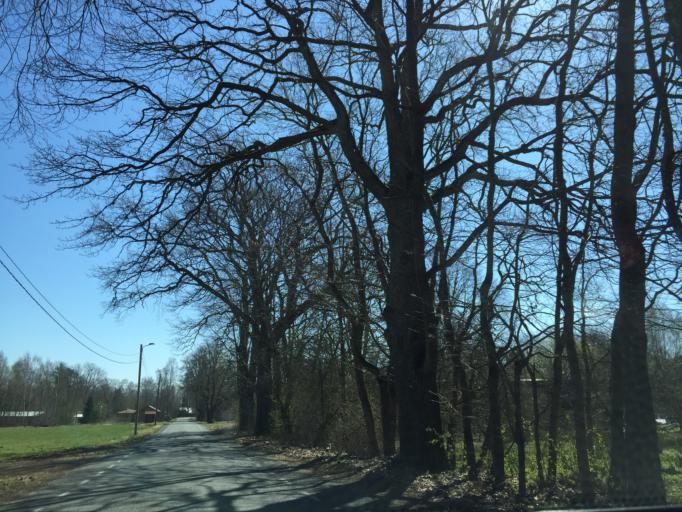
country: EE
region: Jogevamaa
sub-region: Poltsamaa linn
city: Poltsamaa
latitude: 58.3719
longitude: 25.9537
